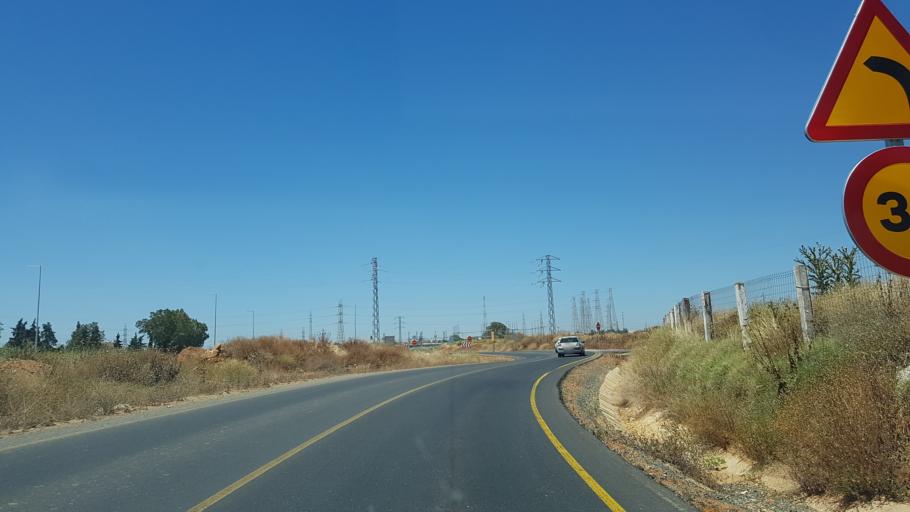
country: ES
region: Andalusia
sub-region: Provincia de Sevilla
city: Dos Hermanas
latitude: 37.3011
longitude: -5.8987
